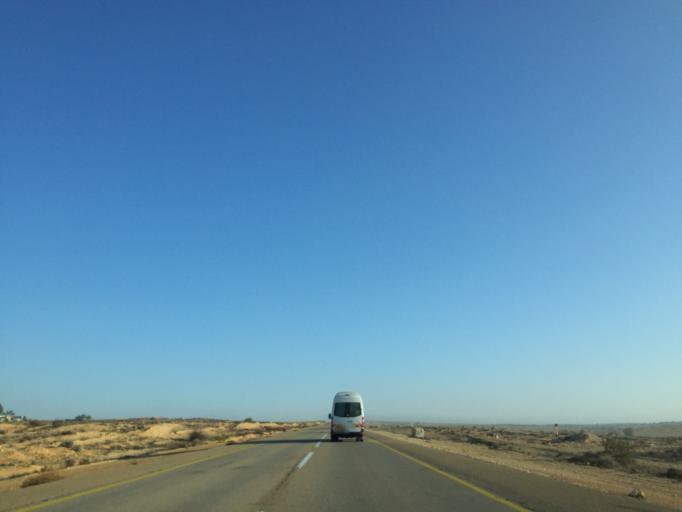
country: IL
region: Southern District
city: Yeroham
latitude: 31.0181
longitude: 34.9627
